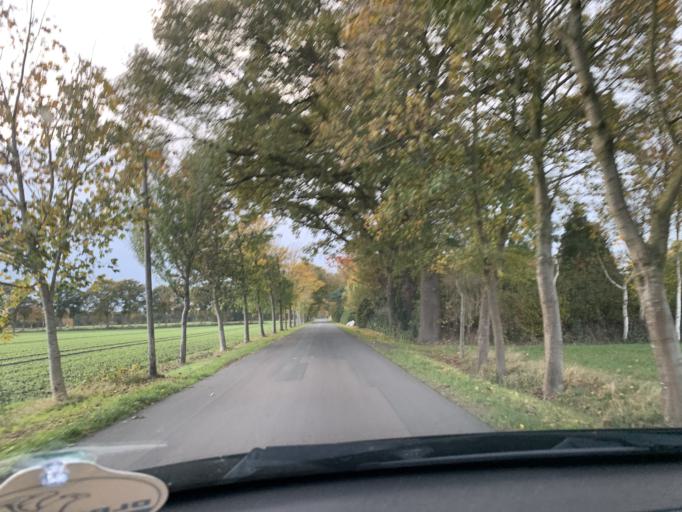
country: DE
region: Lower Saxony
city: Wiefelstede
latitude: 53.2635
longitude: 8.0943
